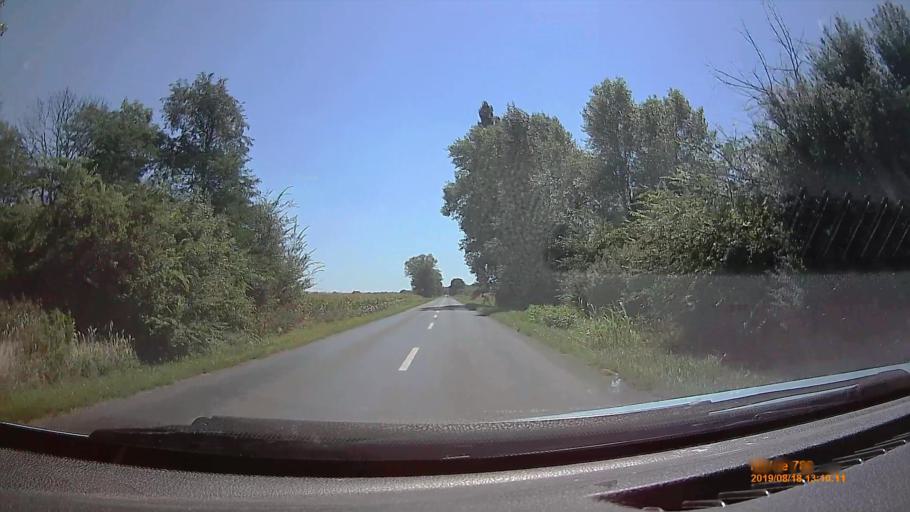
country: HU
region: Fejer
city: Kaloz
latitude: 46.9180
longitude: 18.5156
